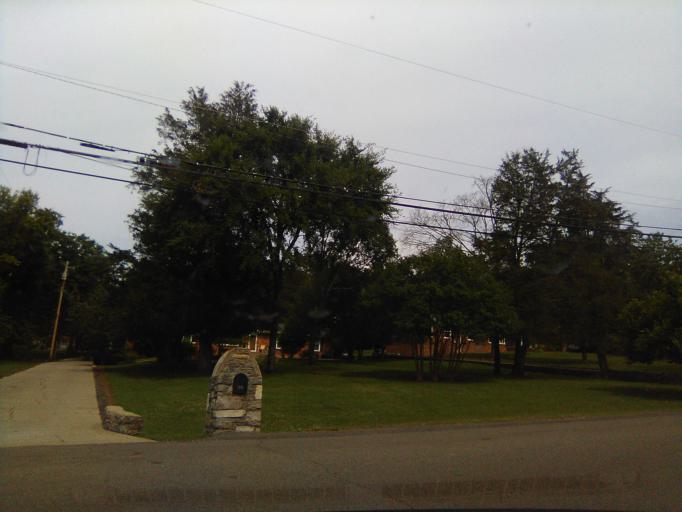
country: US
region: Tennessee
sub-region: Davidson County
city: Belle Meade
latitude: 36.1158
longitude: -86.8957
